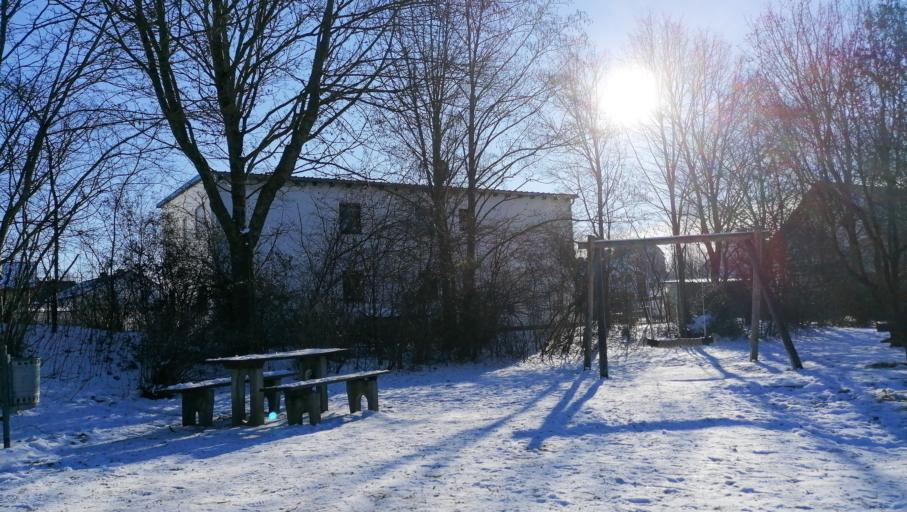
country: DE
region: Bavaria
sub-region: Lower Bavaria
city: Ergolding
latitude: 48.5594
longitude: 12.1410
